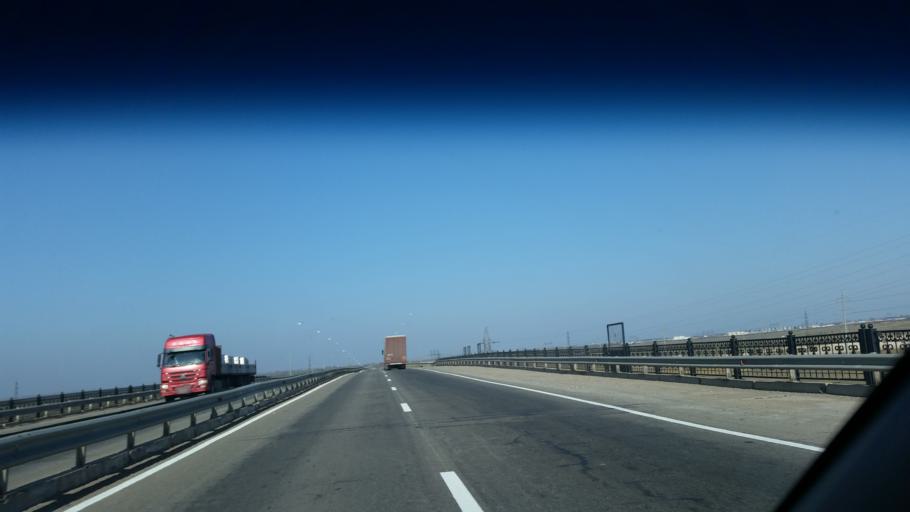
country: KZ
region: Astana Qalasy
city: Astana
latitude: 51.2278
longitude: 71.3257
